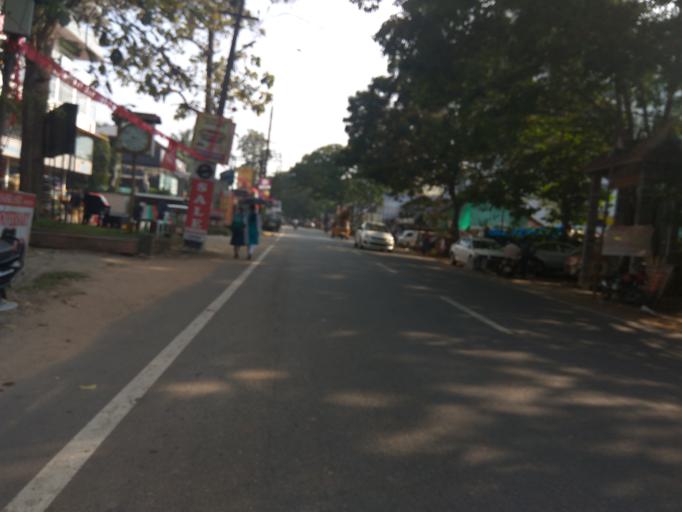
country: IN
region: Kerala
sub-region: Kozhikode
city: Kozhikode
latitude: 11.2819
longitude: 75.7700
